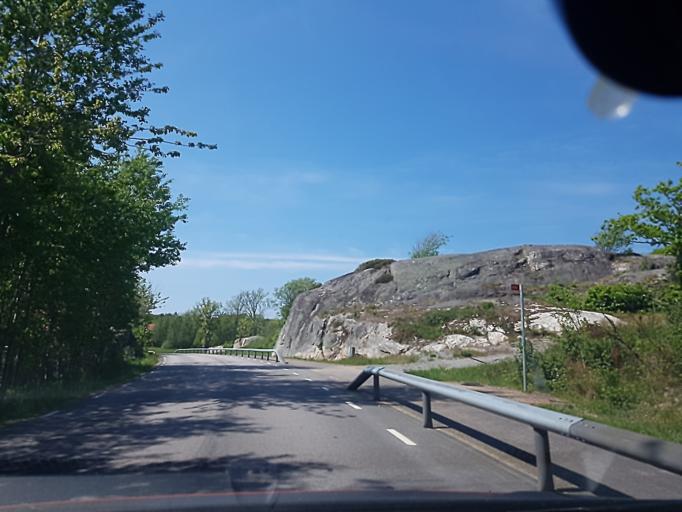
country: SE
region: Vaestra Goetaland
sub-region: Lysekils Kommun
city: Lysekil
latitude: 58.1685
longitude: 11.4322
